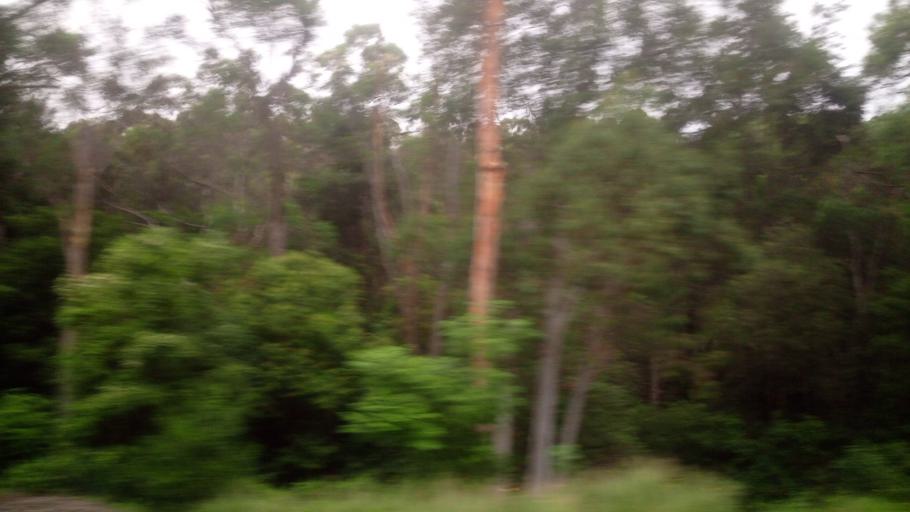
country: AU
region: New South Wales
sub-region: Blue Mountains Municipality
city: Blaxland
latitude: -33.7531
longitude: 150.6085
